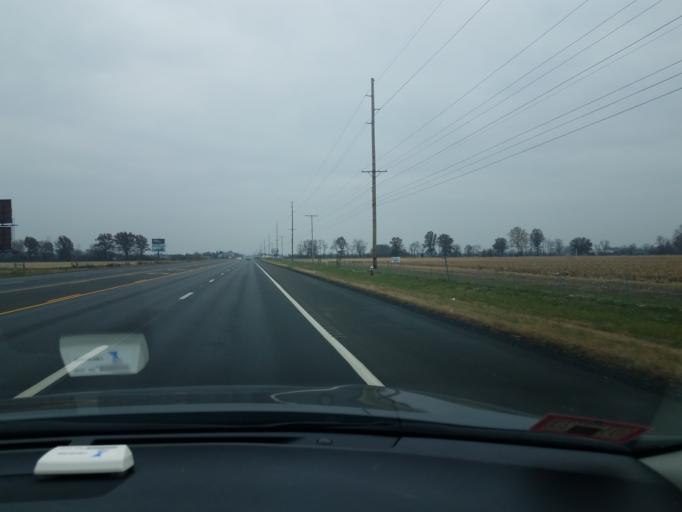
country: US
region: Ohio
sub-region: Erie County
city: Milan
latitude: 41.3665
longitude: -82.6392
